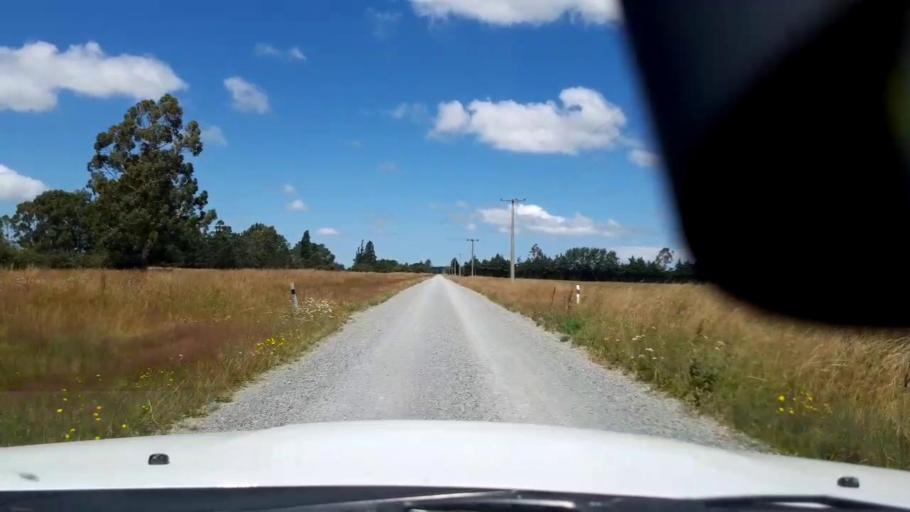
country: NZ
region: Canterbury
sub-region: Timaru District
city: Pleasant Point
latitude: -43.9800
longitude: 171.2859
